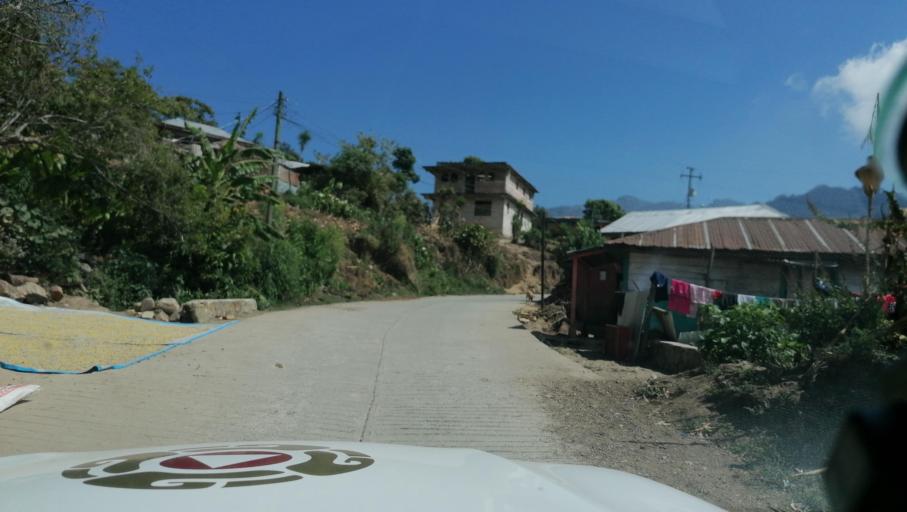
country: GT
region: San Marcos
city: Tacana
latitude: 15.2050
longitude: -92.2057
